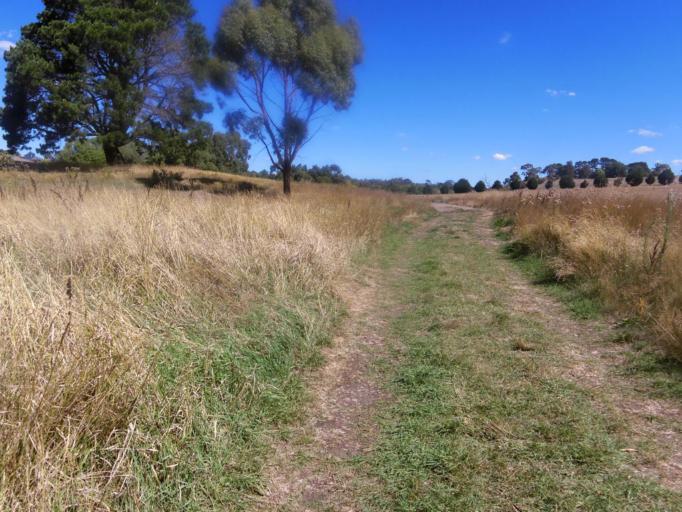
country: AU
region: Victoria
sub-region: Mount Alexander
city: Castlemaine
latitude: -37.2461
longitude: 144.4418
